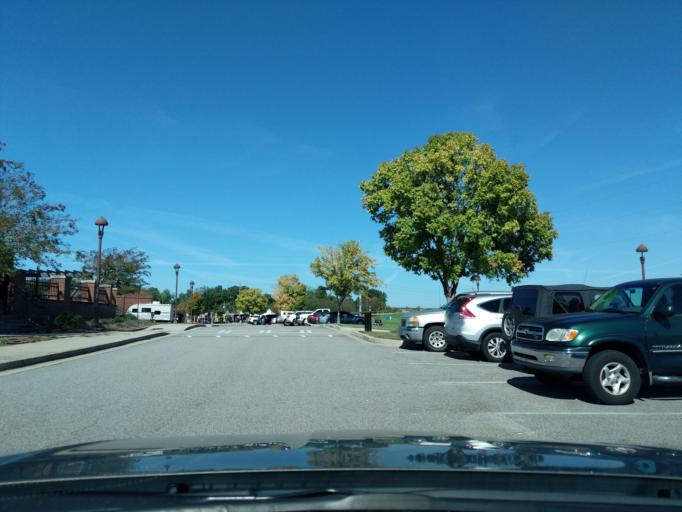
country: US
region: Georgia
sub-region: Richmond County
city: Augusta
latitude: 33.4858
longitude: -81.9940
